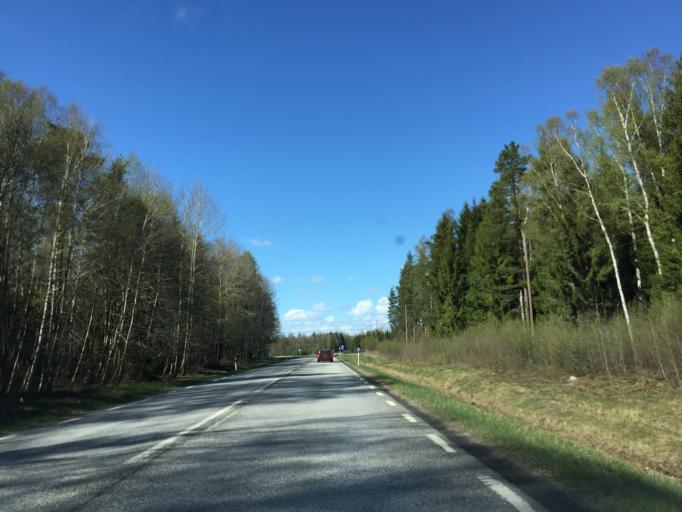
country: SE
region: OErebro
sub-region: Hallsbergs Kommun
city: Skollersta
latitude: 59.1397
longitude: 15.2775
